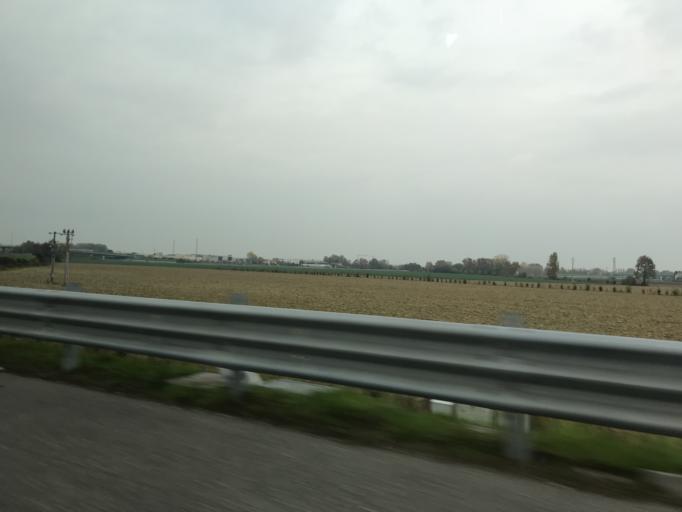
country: IT
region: Veneto
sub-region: Provincia di Venezia
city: Marcon-Gaggio-Colmello
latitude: 45.5797
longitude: 12.2922
